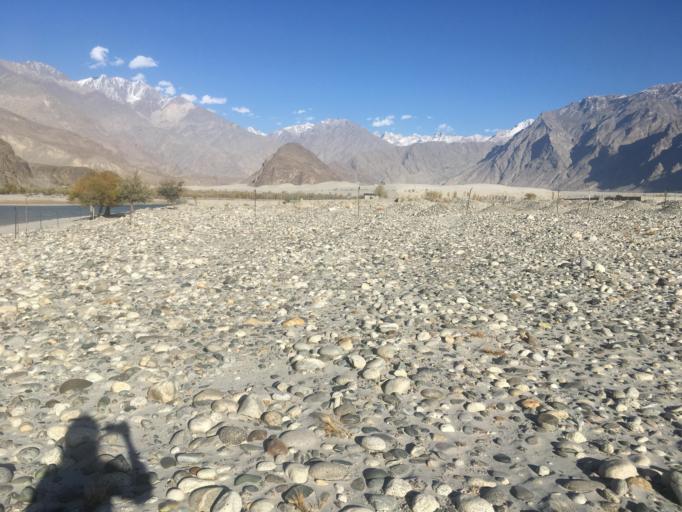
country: PK
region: Gilgit-Baltistan
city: Skardu
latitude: 35.3188
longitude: 75.6892
